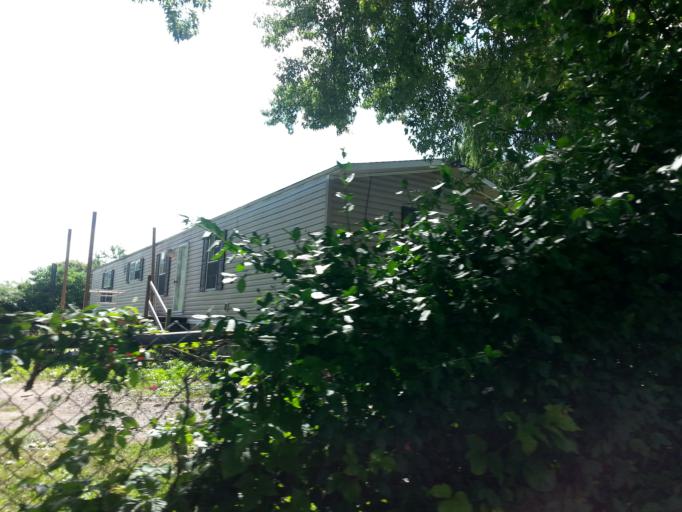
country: US
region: Kentucky
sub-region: Harlan County
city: Cumberland
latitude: 36.9442
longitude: -83.1176
